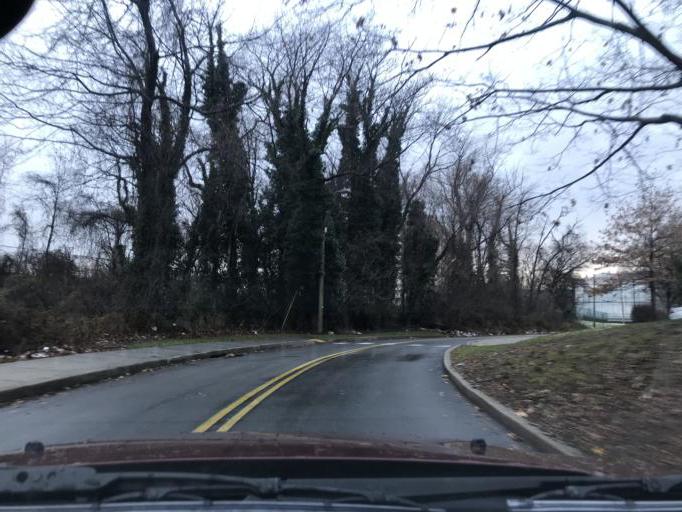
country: US
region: Pennsylvania
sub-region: Montgomery County
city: Bala-Cynwyd
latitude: 40.0049
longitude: -75.2123
